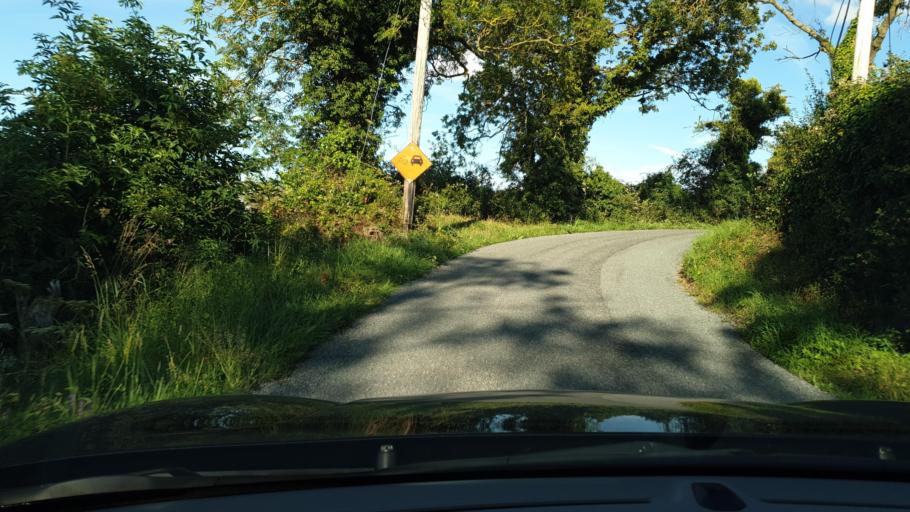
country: IE
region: Leinster
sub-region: An Mhi
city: Stamullin
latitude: 53.5801
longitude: -6.2422
